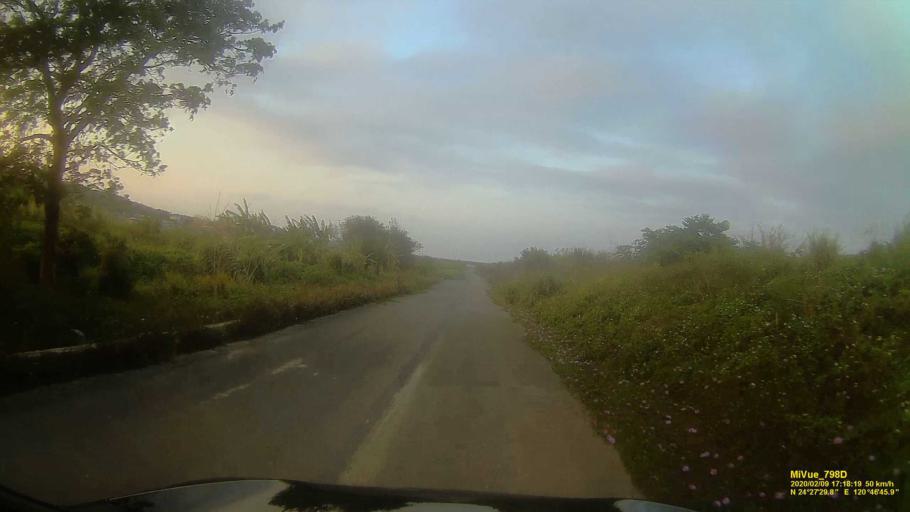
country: TW
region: Taiwan
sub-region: Miaoli
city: Miaoli
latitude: 24.4585
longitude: 120.7794
